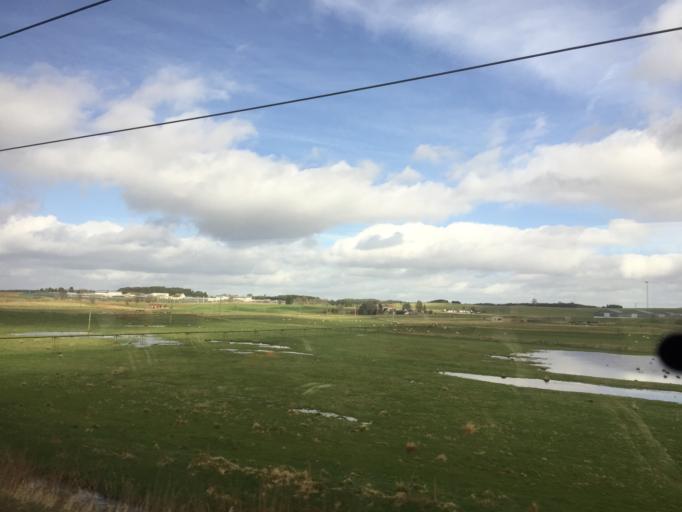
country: GB
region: Scotland
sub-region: South Lanarkshire
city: Carnwath
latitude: 55.6850
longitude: -3.6574
